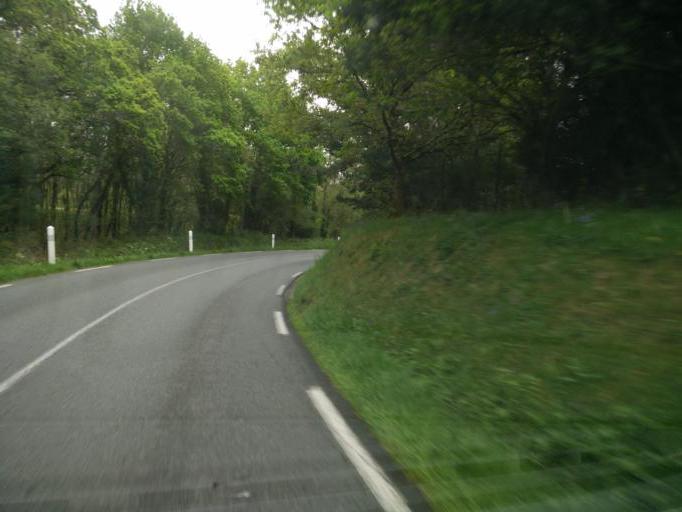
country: FR
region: Brittany
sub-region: Departement des Cotes-d'Armor
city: Locquemeau
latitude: 48.6930
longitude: -3.5529
